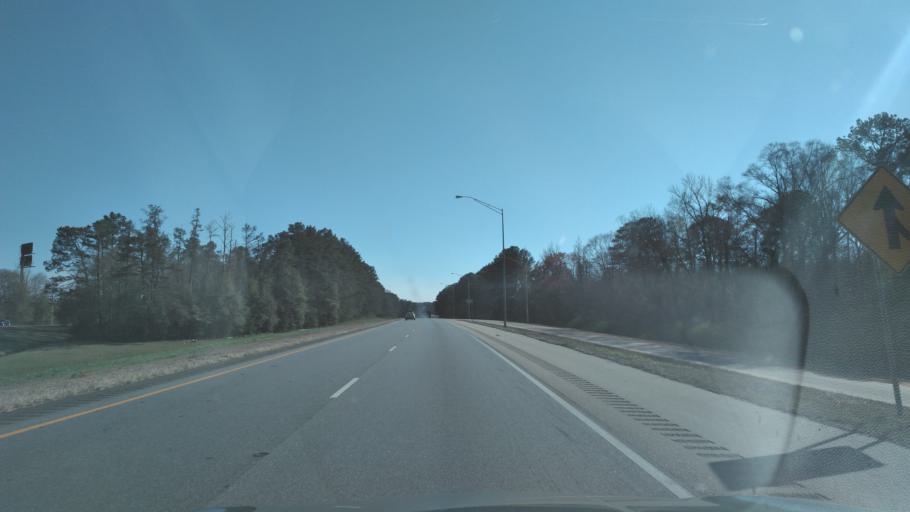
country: US
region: Alabama
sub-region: Butler County
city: Greenville
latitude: 31.8225
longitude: -86.6653
